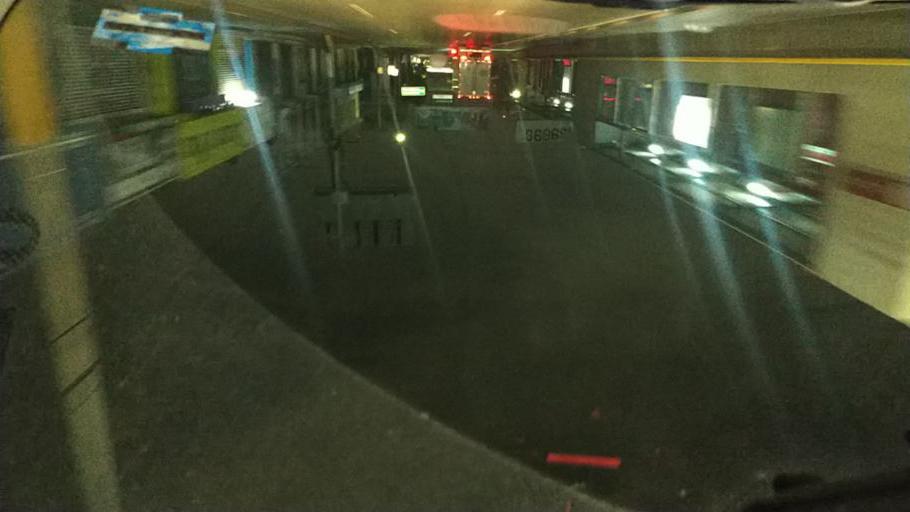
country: MX
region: Mexico
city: Ecatepec
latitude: 19.6246
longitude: -99.0766
